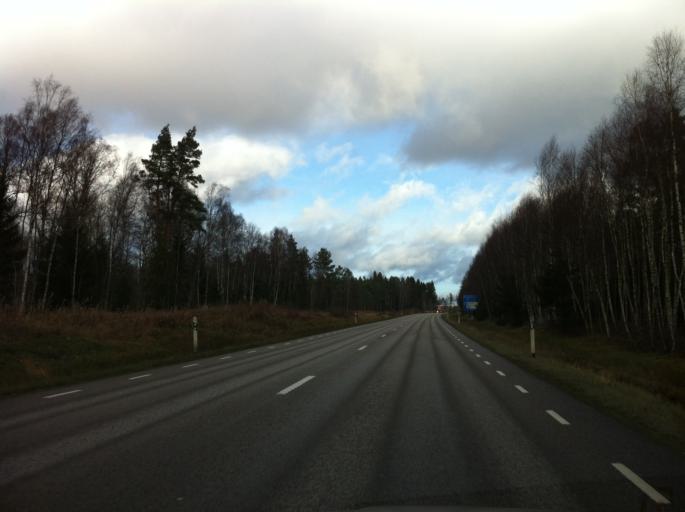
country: SE
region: Kronoberg
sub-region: Almhults Kommun
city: AElmhult
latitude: 56.5228
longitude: 14.1402
